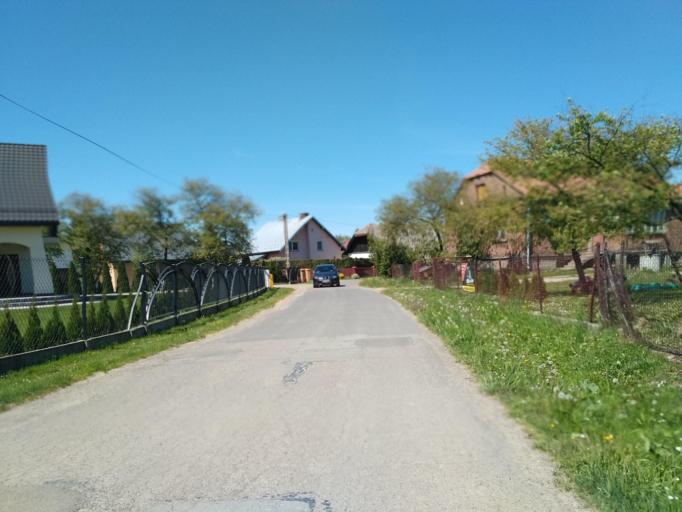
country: PL
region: Subcarpathian Voivodeship
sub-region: Powiat brzozowski
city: Gorki
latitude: 49.6493
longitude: 22.0305
